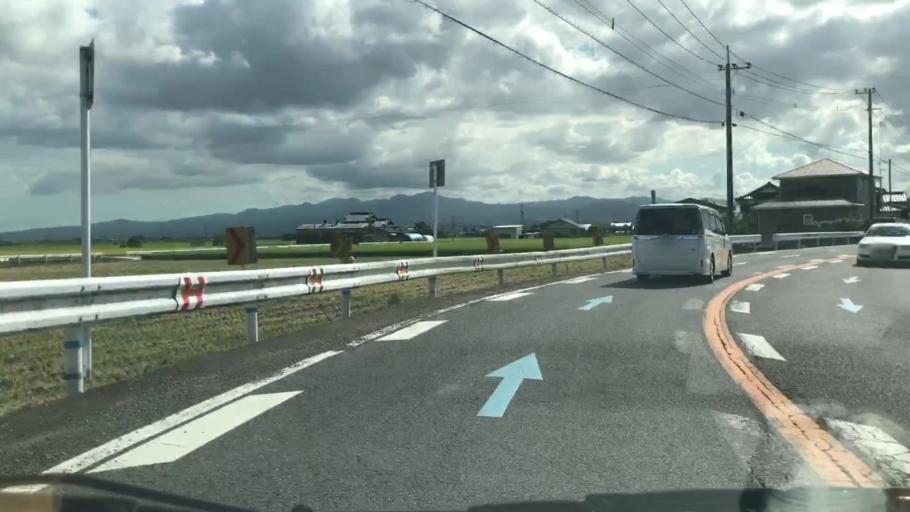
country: JP
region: Saga Prefecture
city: Kashima
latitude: 33.1629
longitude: 130.1682
